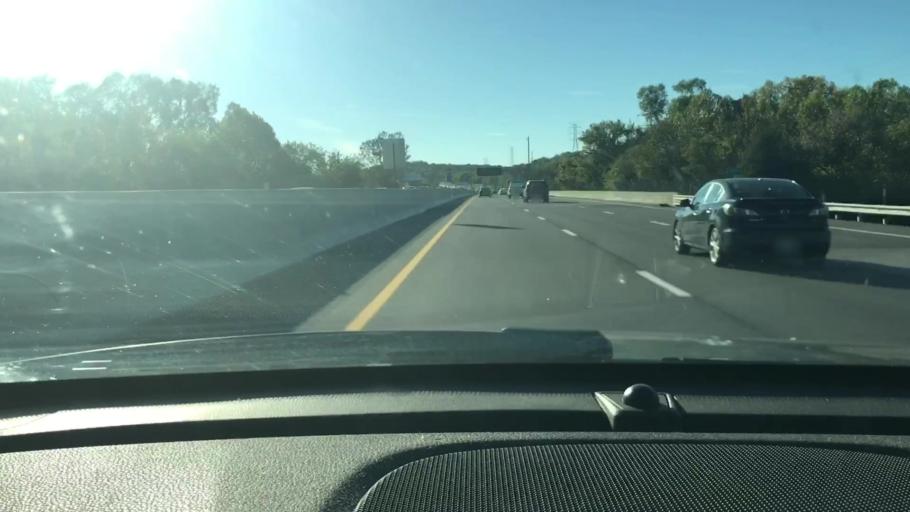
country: US
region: Tennessee
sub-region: Davidson County
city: Goodlettsville
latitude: 36.3123
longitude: -86.6716
